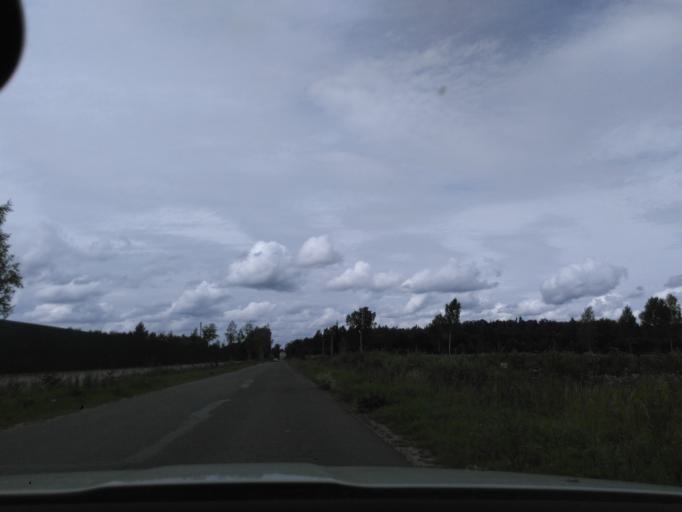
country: RU
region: Tverskaya
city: Konakovo
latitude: 56.6783
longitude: 36.7089
